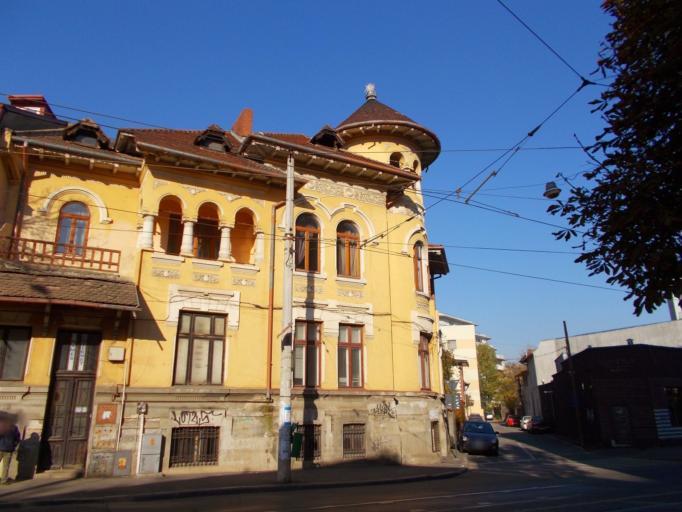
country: RO
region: Bucuresti
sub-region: Municipiul Bucuresti
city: Bucuresti
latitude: 44.4194
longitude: 26.0950
